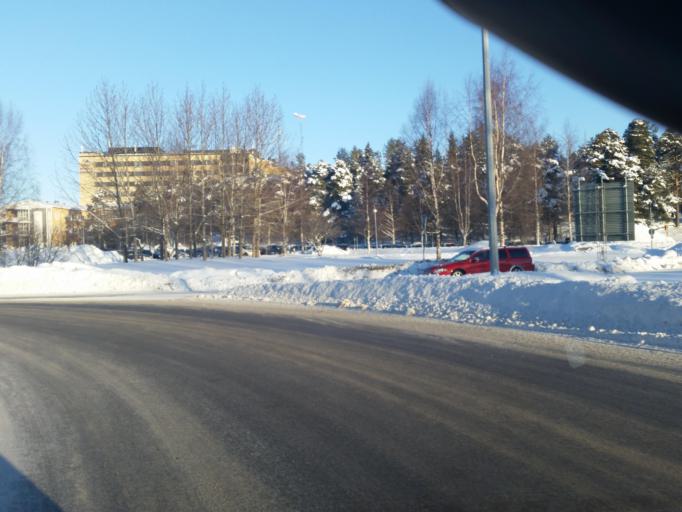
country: SE
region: Norrbotten
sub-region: Pitea Kommun
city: Pitea
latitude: 65.3103
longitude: 21.4966
